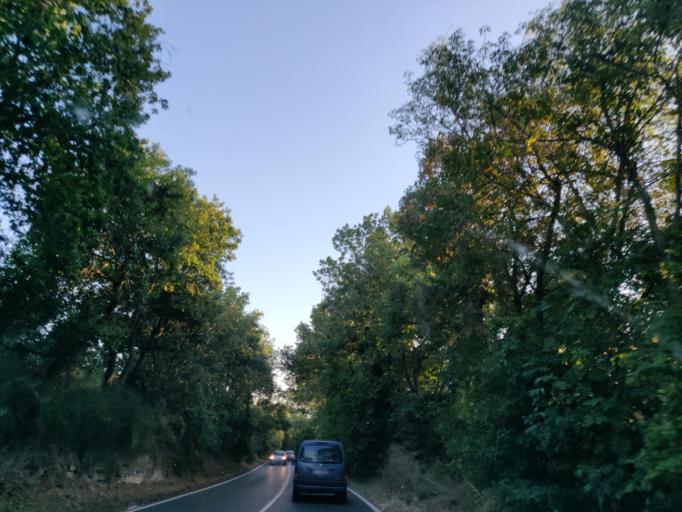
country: IT
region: Latium
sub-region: Provincia di Viterbo
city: Canino
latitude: 42.4415
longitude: 11.7308
